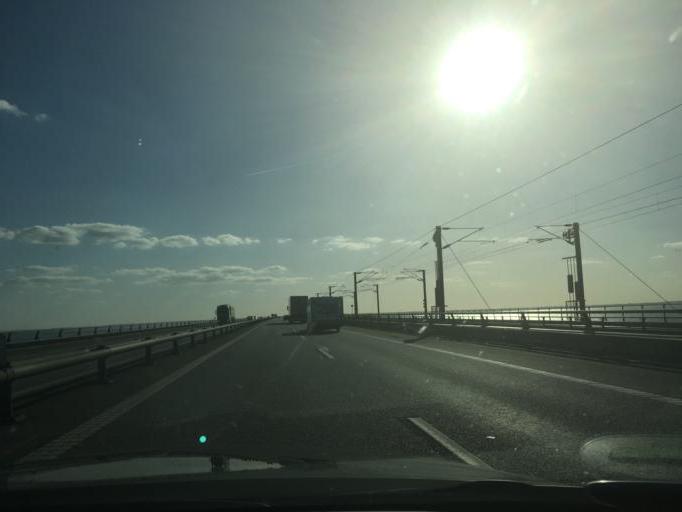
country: DK
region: South Denmark
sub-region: Nyborg Kommune
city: Nyborg
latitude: 55.3198
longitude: 10.9333
